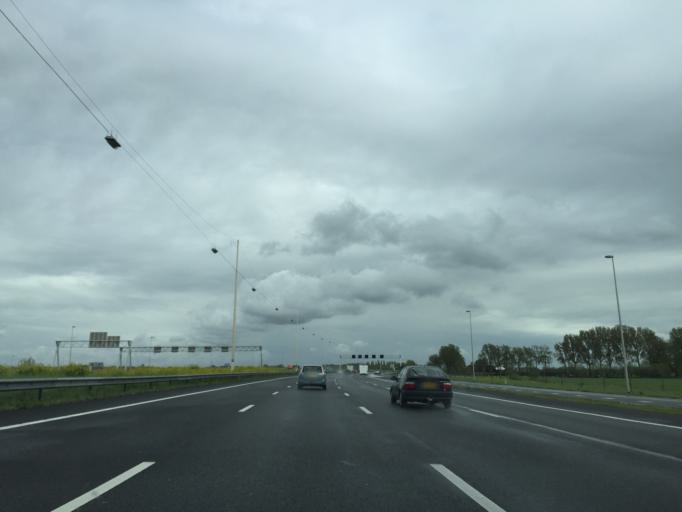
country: NL
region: Utrecht
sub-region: Gemeente Montfoort
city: Montfoort
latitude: 52.0804
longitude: 4.9878
